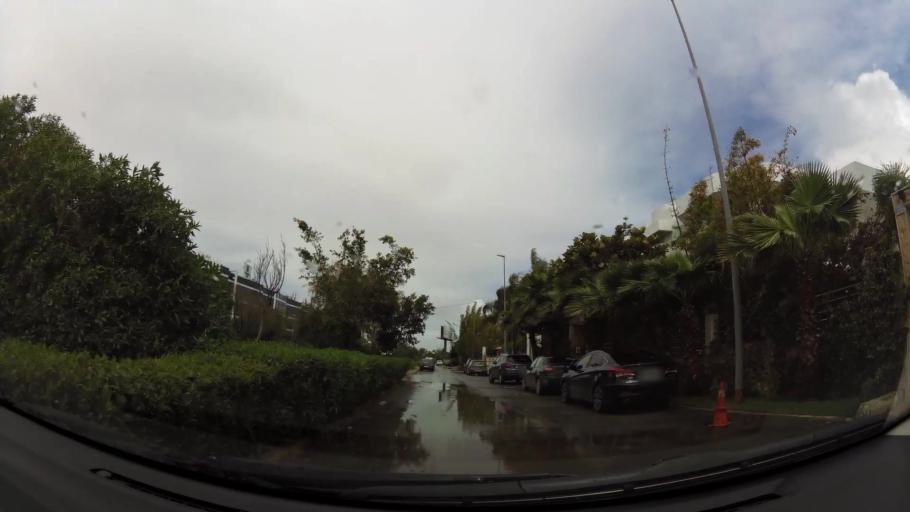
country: MA
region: Grand Casablanca
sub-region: Casablanca
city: Casablanca
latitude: 33.5340
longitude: -7.6406
